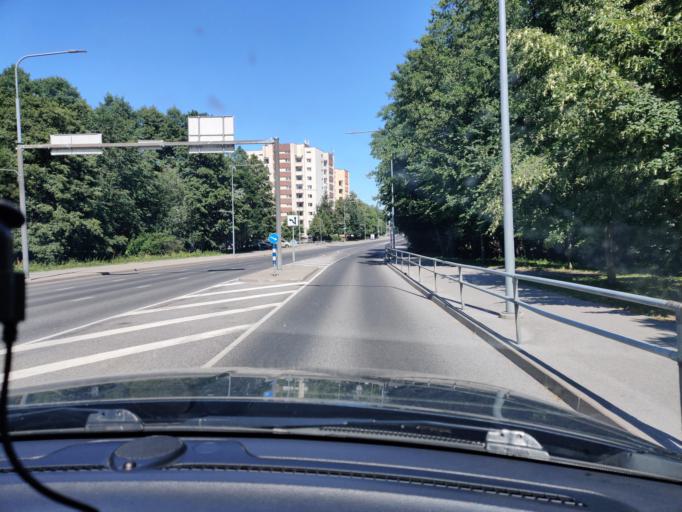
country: EE
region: Harju
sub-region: Tallinna linn
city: Tallinn
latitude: 59.4036
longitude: 24.7084
